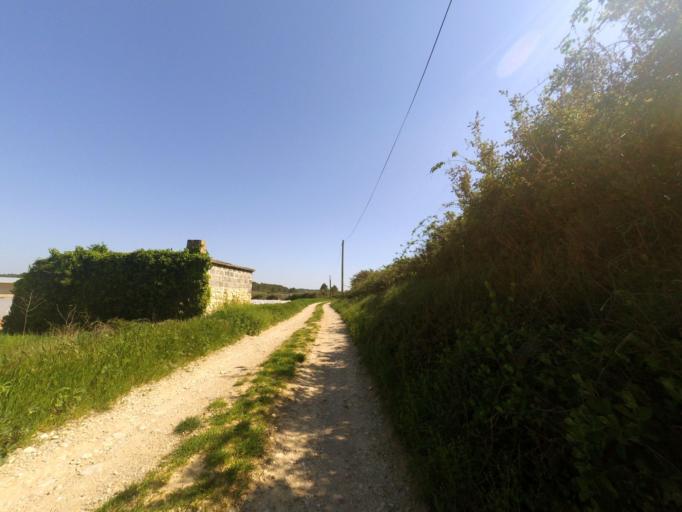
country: FR
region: Languedoc-Roussillon
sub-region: Departement du Gard
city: Calvisson
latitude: 43.7631
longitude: 4.1990
